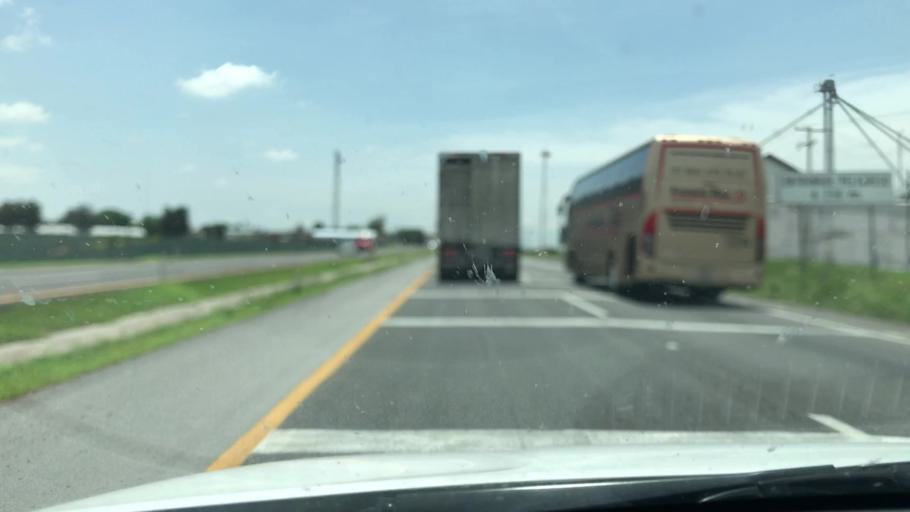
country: MX
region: Guanajuato
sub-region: Penjamo
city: Mezquite de Luna
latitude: 20.3787
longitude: -101.8407
